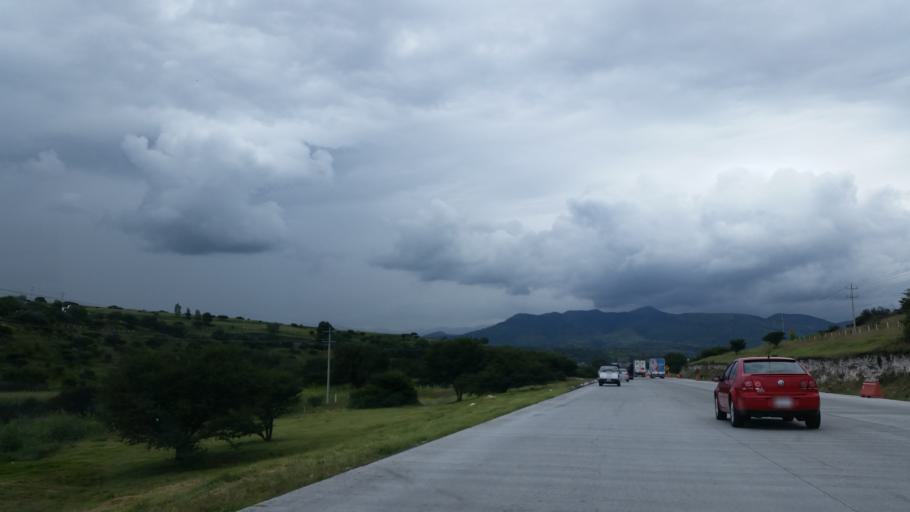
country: MX
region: Hidalgo
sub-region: Tepeji del Rio de Ocampo
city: Cantera de Villagran
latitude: 19.8630
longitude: -99.3138
